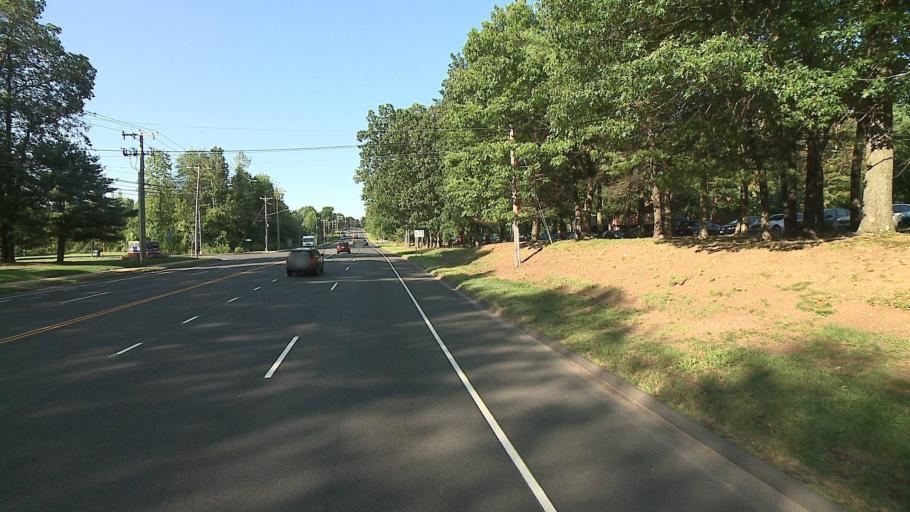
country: US
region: Connecticut
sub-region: Hartford County
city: Farmington
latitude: 41.7350
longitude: -72.7960
